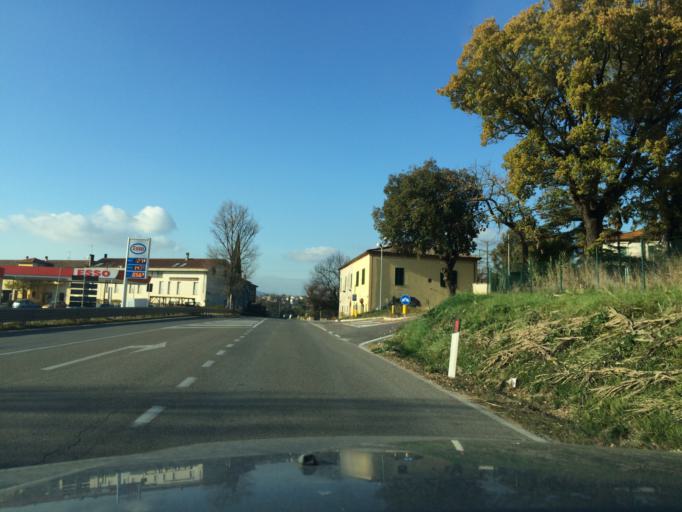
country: IT
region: Umbria
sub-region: Provincia di Terni
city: Fornole
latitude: 42.5458
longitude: 12.4503
